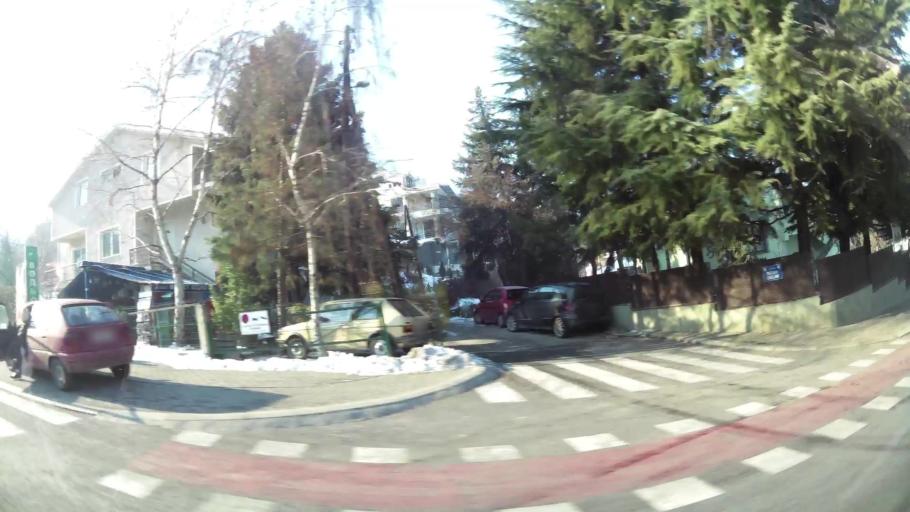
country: MK
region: Karpos
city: Skopje
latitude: 41.9847
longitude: 21.4187
